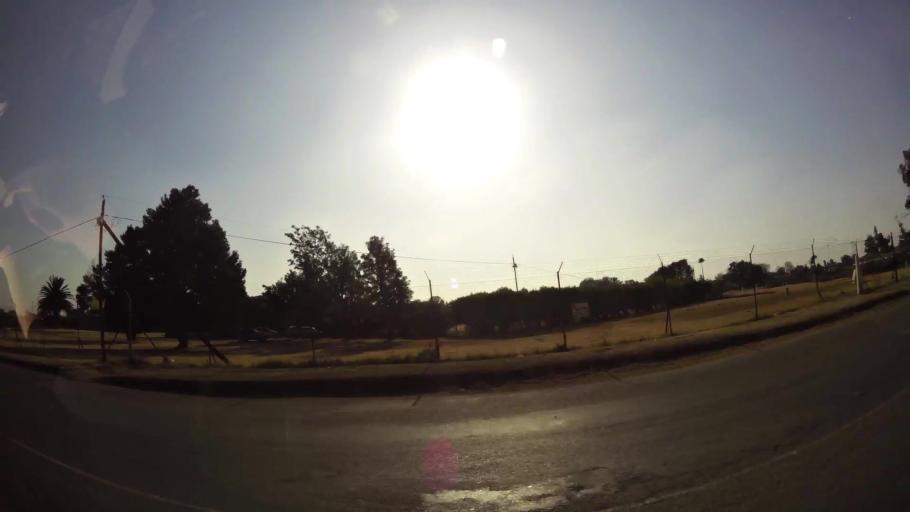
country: ZA
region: Gauteng
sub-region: West Rand District Municipality
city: Randfontein
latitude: -26.1560
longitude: 27.7164
